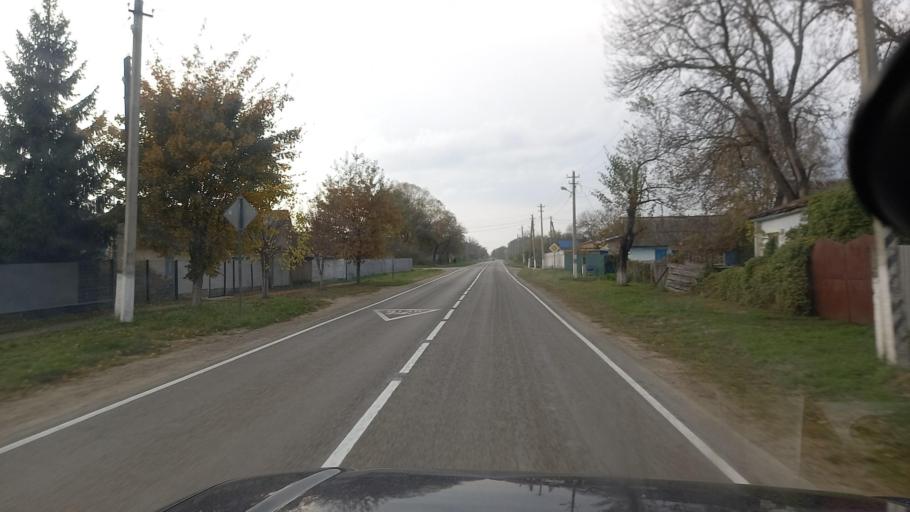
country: RU
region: Krasnodarskiy
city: Gubskaya
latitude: 44.3174
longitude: 40.6257
